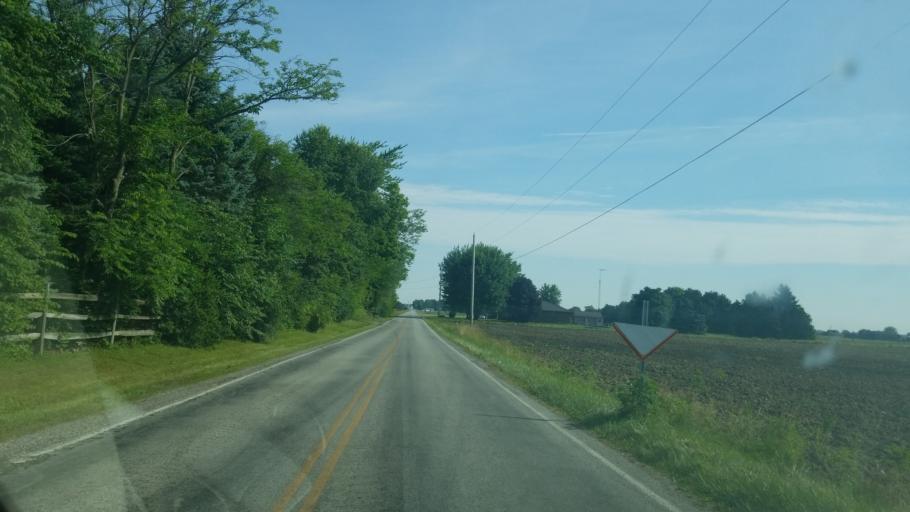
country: US
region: Ohio
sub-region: Hancock County
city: Findlay
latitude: 41.0004
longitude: -83.5881
